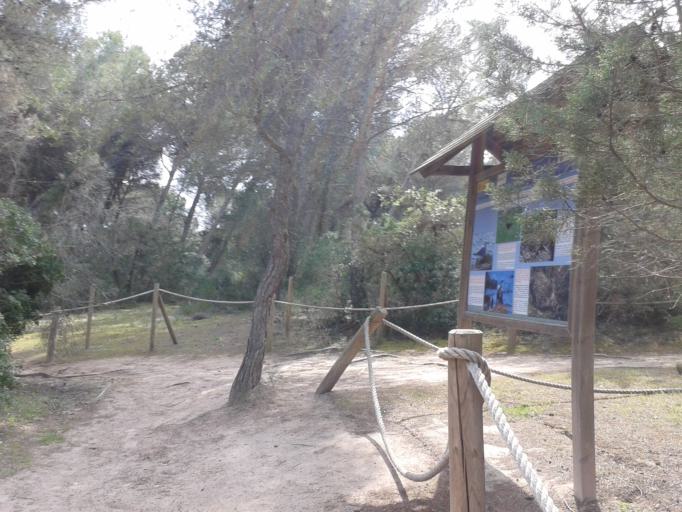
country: ES
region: Balearic Islands
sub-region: Illes Balears
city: Son Servera
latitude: 39.5820
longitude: 3.3837
